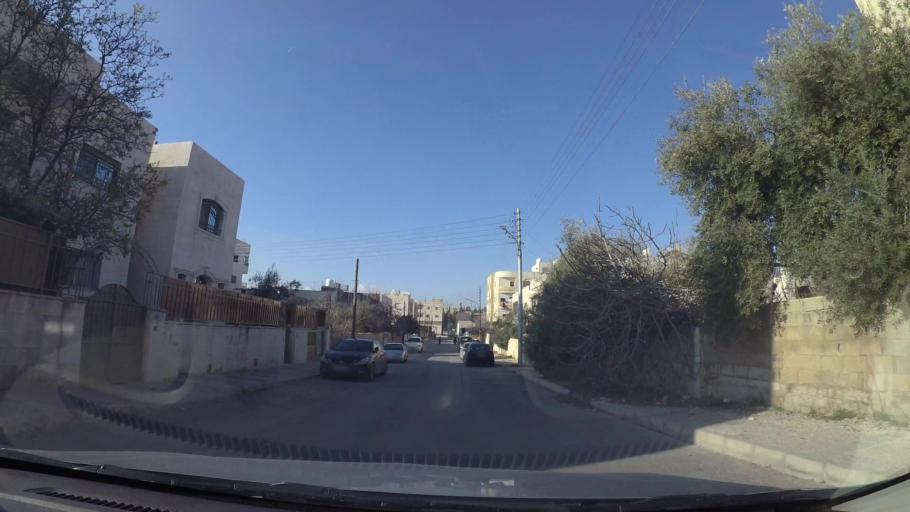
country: JO
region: Amman
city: Al Bunayyat ash Shamaliyah
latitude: 31.9009
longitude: 35.9099
